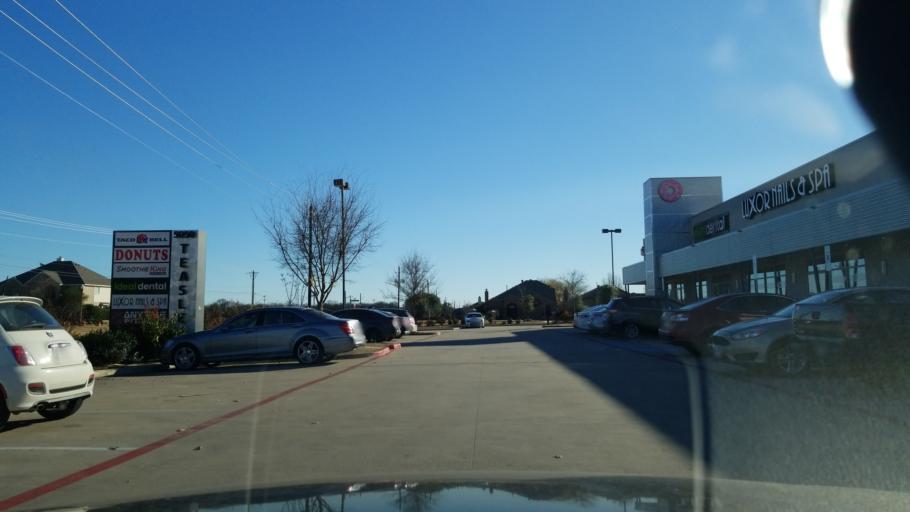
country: US
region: Texas
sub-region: Denton County
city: Corinth
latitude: 33.1444
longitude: -97.1057
